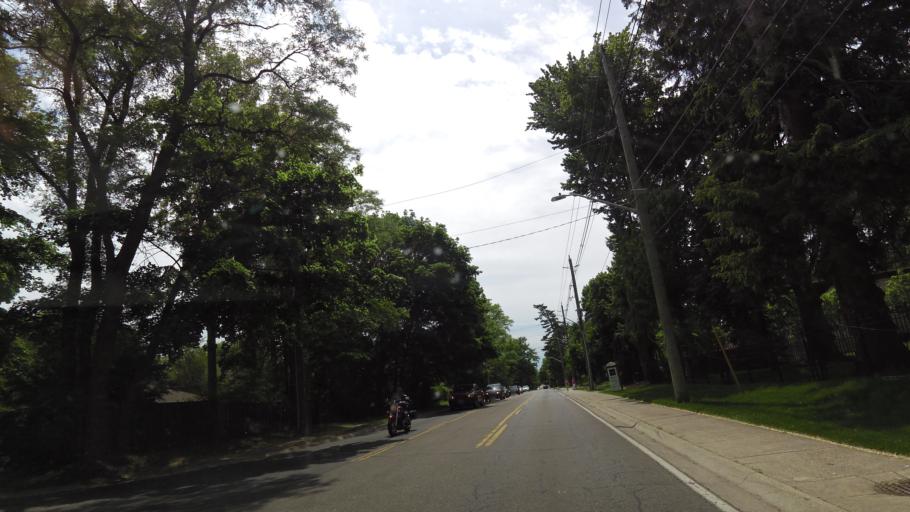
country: CA
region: Ontario
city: Oakville
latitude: 43.4653
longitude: -79.6472
